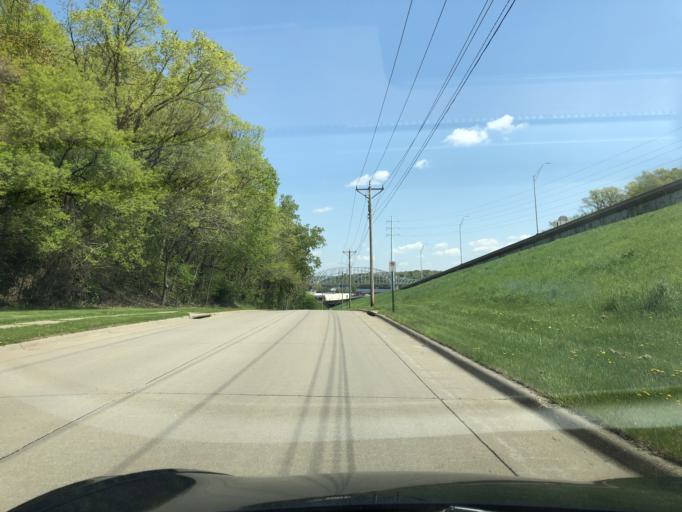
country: US
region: Iowa
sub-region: Dubuque County
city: Dubuque
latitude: 42.4830
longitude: -90.6664
